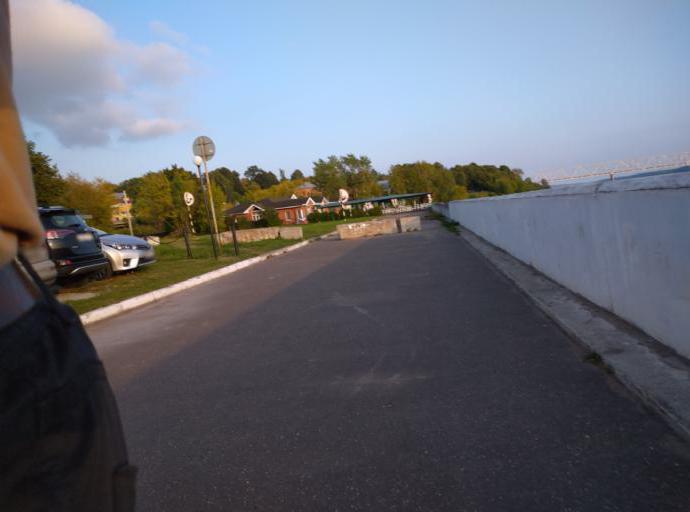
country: RU
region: Kostroma
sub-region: Kostromskoy Rayon
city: Kostroma
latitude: 57.7501
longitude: 40.9518
